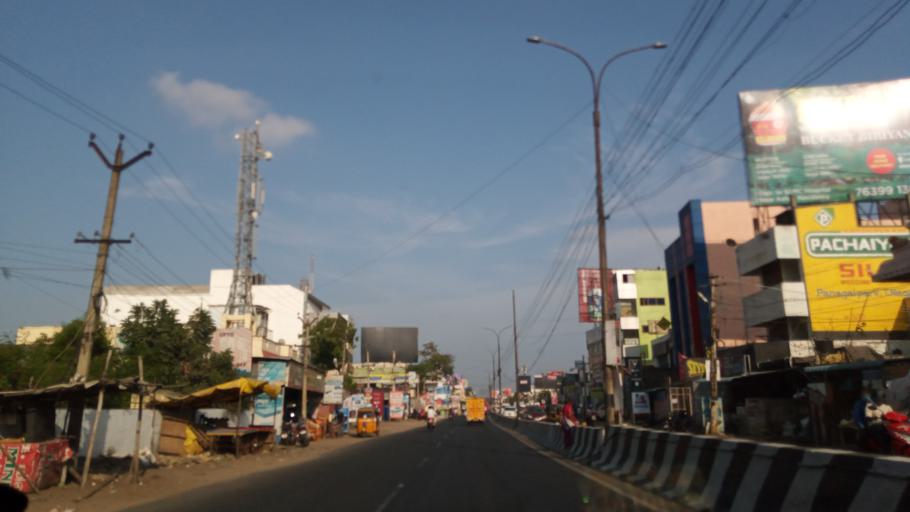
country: IN
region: Tamil Nadu
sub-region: Kancheepuram
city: Poonamalle
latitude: 13.0432
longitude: 80.1226
